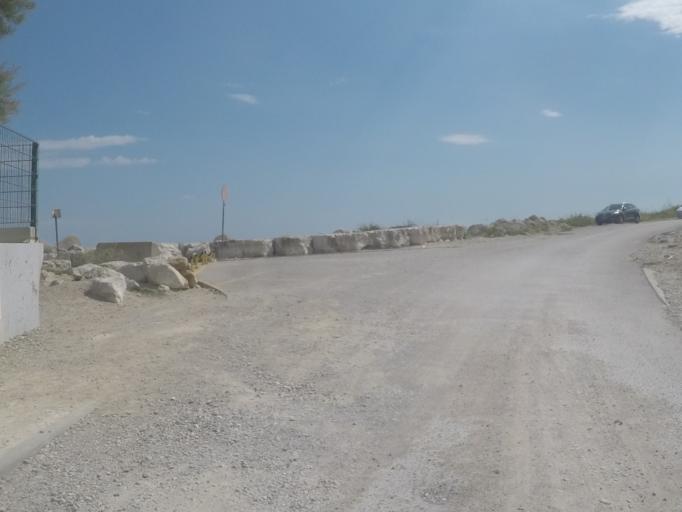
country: PT
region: Setubal
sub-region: Sesimbra
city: Sesimbra
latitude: 38.4347
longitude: -9.1153
